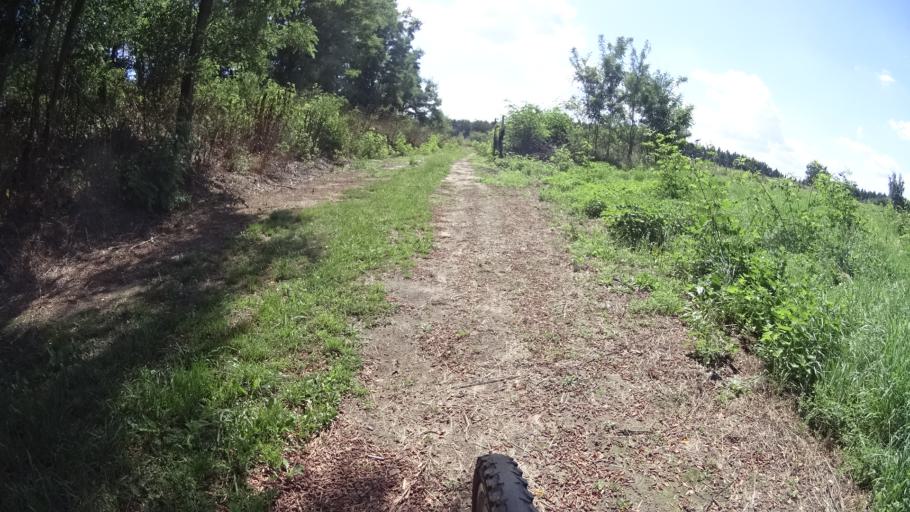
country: PL
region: Masovian Voivodeship
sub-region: Powiat grojecki
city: Mogielnica
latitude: 51.6793
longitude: 20.7519
